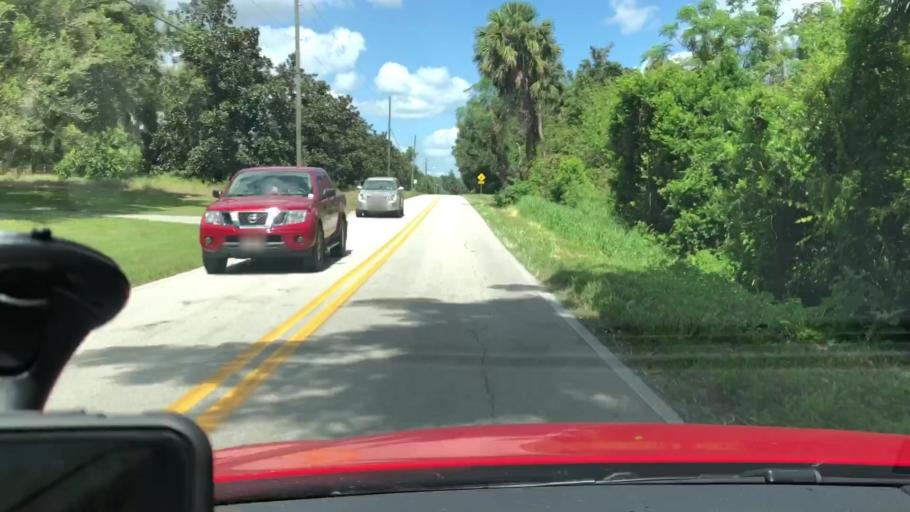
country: US
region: Florida
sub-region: Volusia County
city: North DeLand
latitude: 29.0515
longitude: -81.3166
